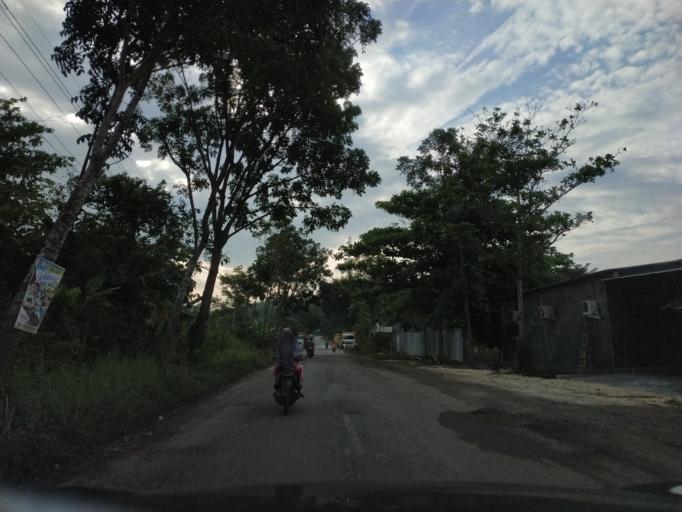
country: ID
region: Central Java
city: Ngampel
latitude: -6.9021
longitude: 111.4424
